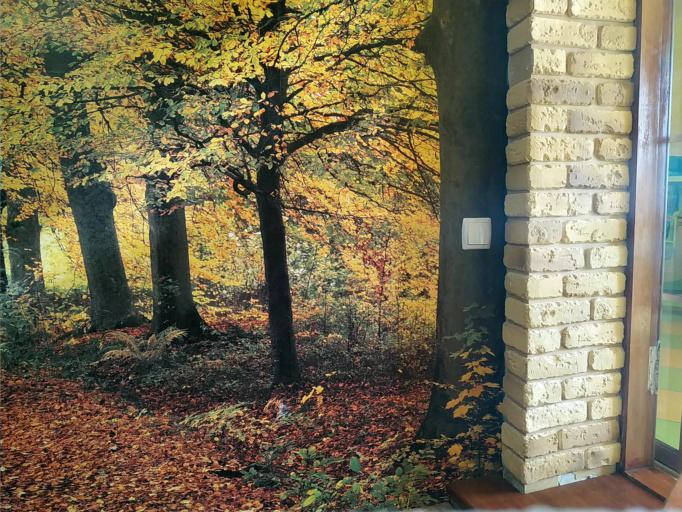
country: RU
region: Smolensk
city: Katyn'
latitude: 55.0108
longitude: 31.7689
